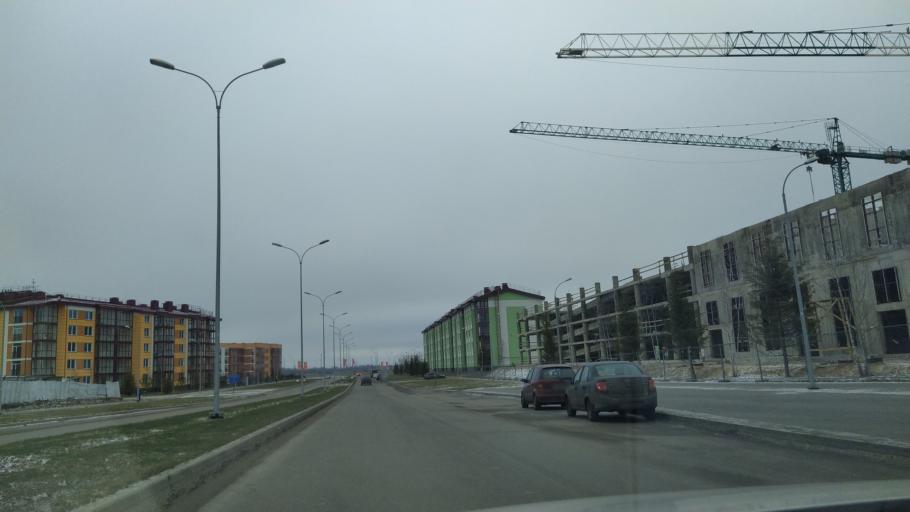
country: RU
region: St.-Petersburg
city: Aleksandrovskaya
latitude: 59.7577
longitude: 30.3681
